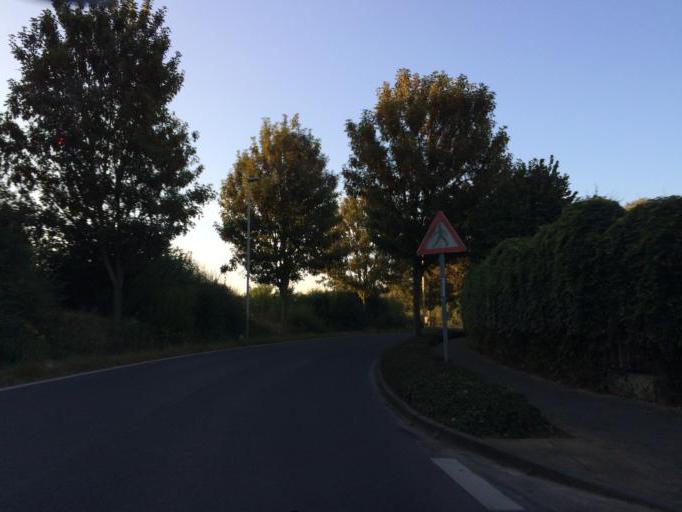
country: DE
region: North Rhine-Westphalia
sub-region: Regierungsbezirk Koln
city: Konigswinter
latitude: 50.6631
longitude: 7.1759
